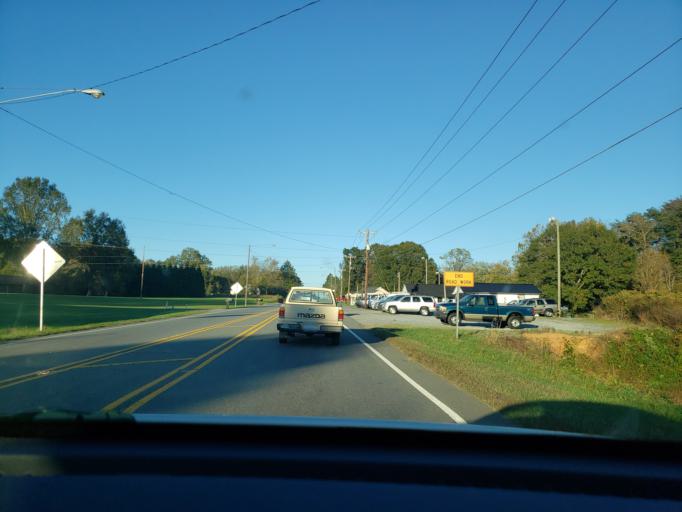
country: US
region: North Carolina
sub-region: Forsyth County
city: Walkertown
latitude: 36.1532
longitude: -80.1492
